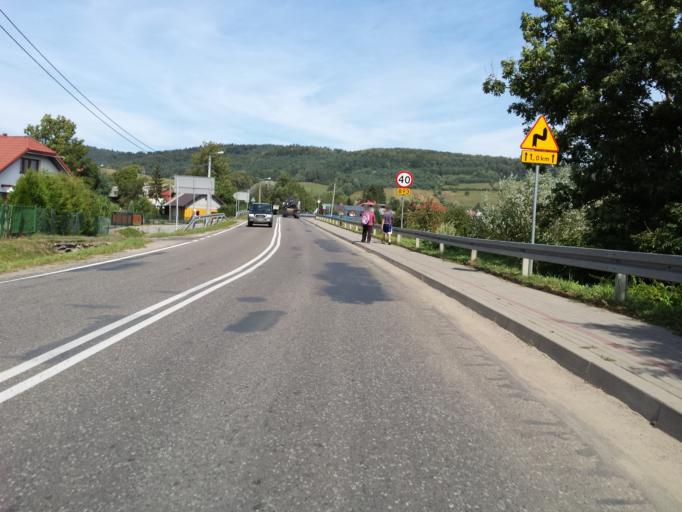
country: PL
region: Subcarpathian Voivodeship
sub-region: Powiat leski
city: Lesko
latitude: 49.4246
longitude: 22.3249
